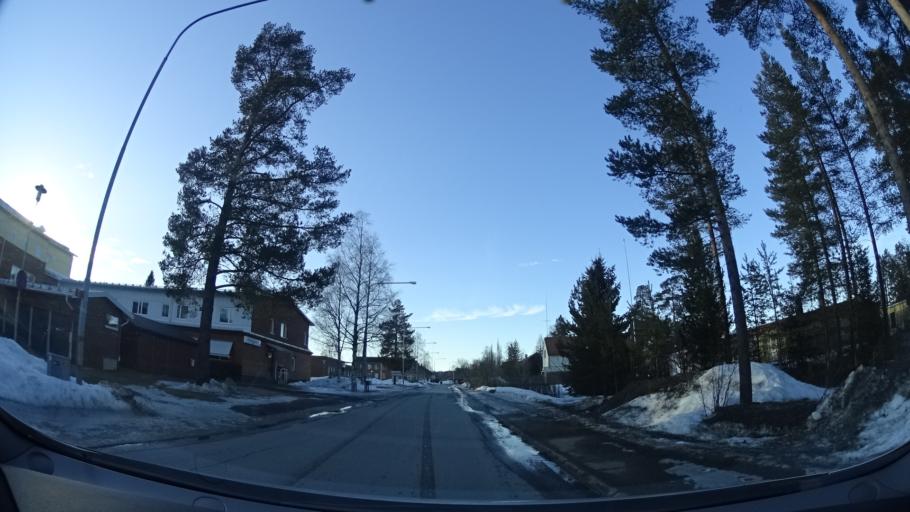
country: SE
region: Vaesterbotten
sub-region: Skelleftea Kommun
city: Byske
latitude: 64.9503
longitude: 21.2071
